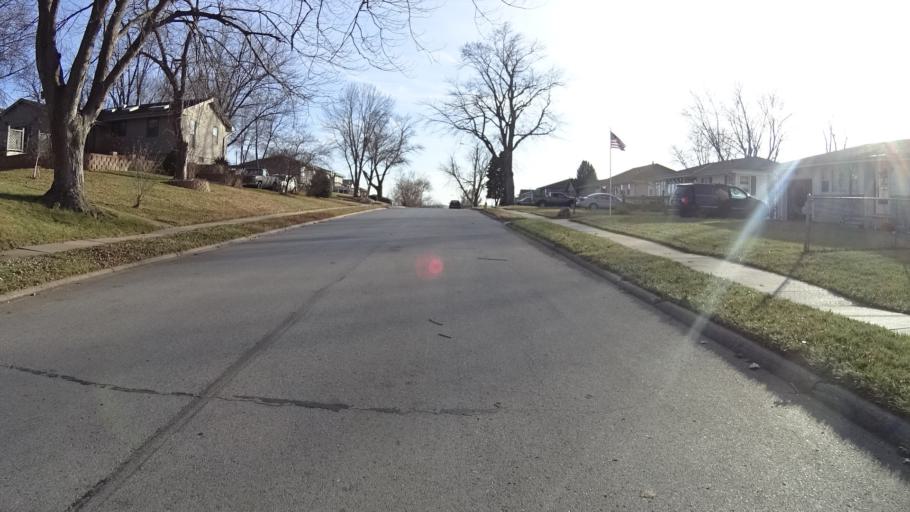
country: US
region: Nebraska
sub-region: Sarpy County
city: La Vista
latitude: 41.1894
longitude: -95.9969
